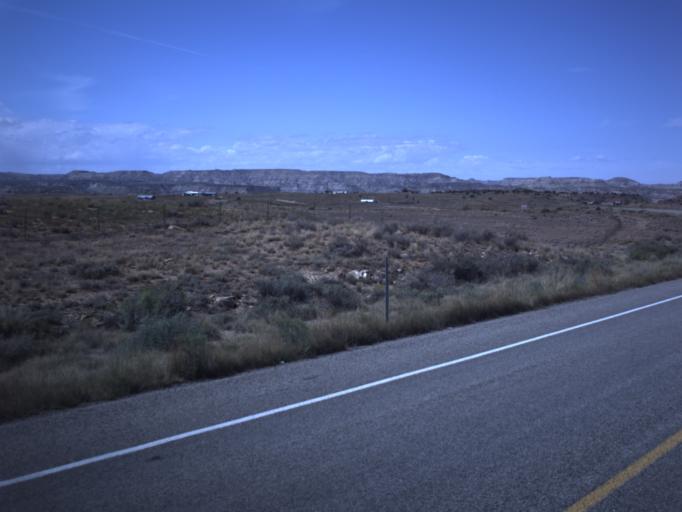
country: US
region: Colorado
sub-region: Montezuma County
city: Towaoc
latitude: 37.1773
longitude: -109.1150
